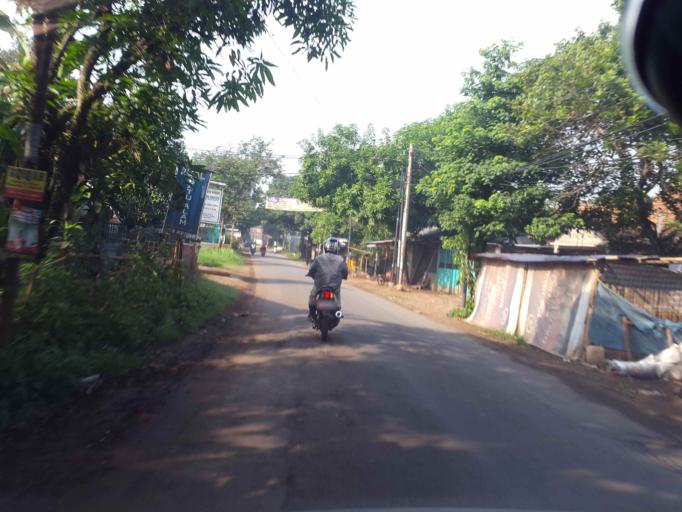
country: ID
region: West Java
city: Cileungsir
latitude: -6.3825
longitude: 106.9890
